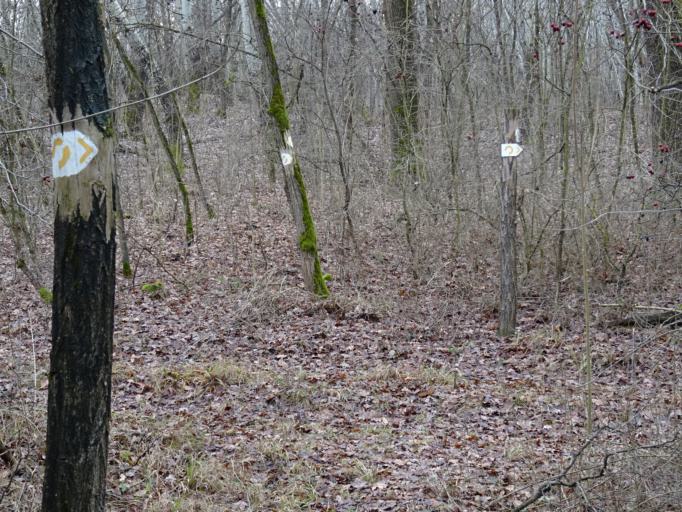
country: HU
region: Bacs-Kiskun
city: Szabadszallas
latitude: 46.8861
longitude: 19.2914
